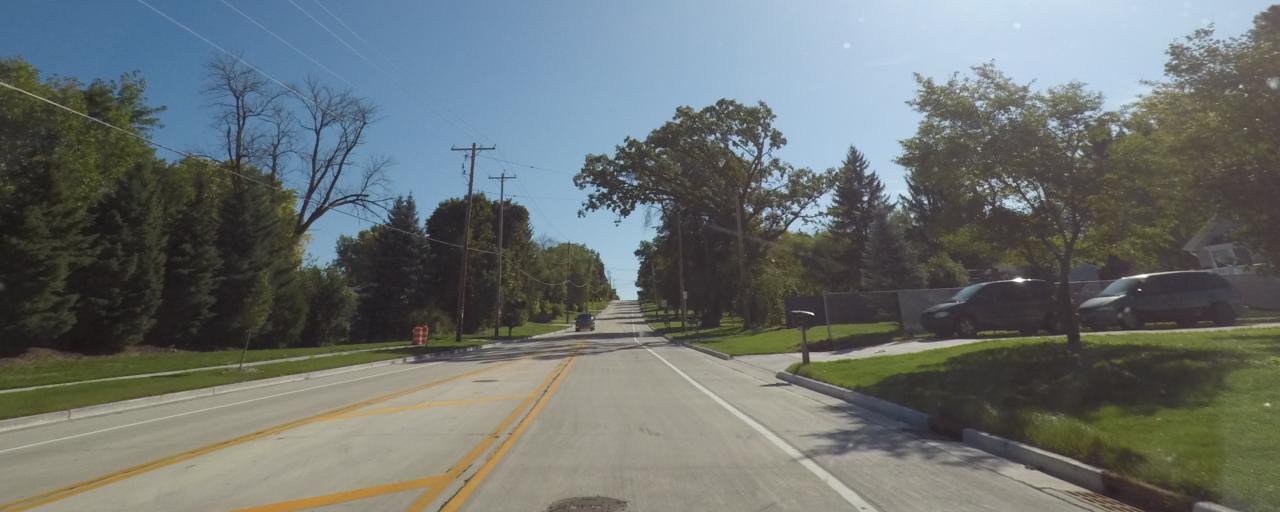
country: US
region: Wisconsin
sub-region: Waukesha County
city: Waukesha
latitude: 43.0321
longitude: -88.2665
